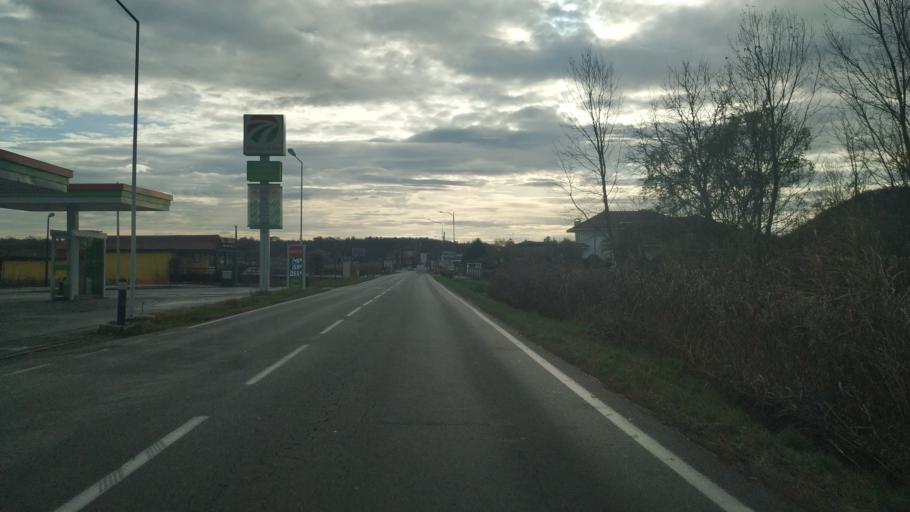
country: IT
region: Piedmont
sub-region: Provincia di Novara
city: Prato Sesia
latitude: 45.6570
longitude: 8.3612
